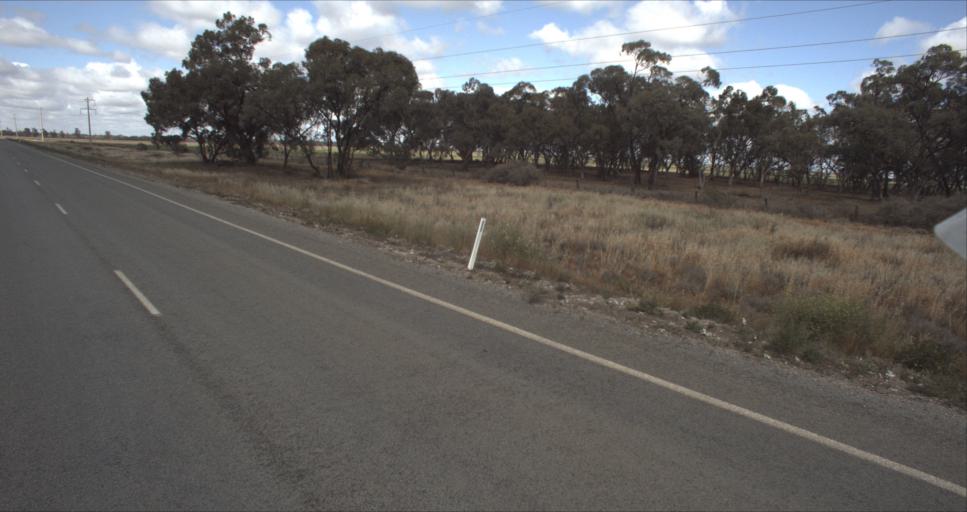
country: AU
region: New South Wales
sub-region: Murrumbidgee Shire
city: Darlington Point
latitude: -34.5760
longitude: 146.1661
